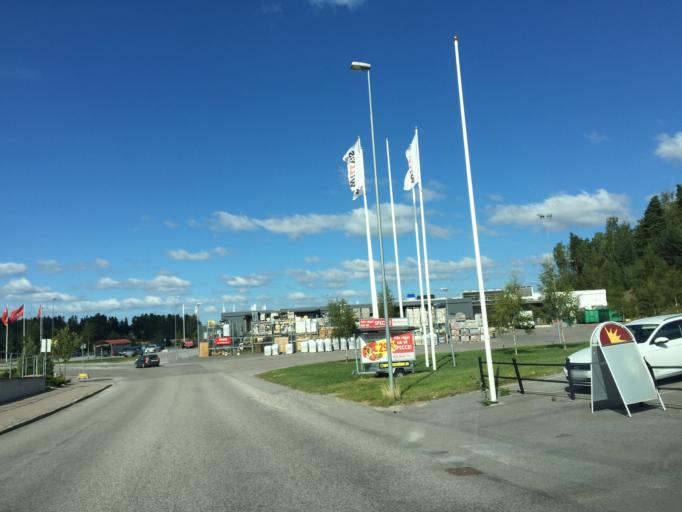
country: SE
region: Soedermanland
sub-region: Katrineholms Kommun
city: Katrineholm
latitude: 59.0027
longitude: 16.2265
